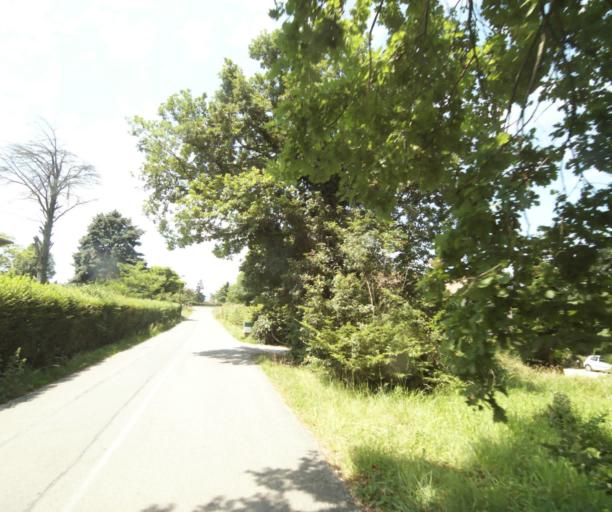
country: FR
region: Rhone-Alpes
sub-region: Departement de la Haute-Savoie
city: Messery
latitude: 46.3530
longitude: 6.3243
